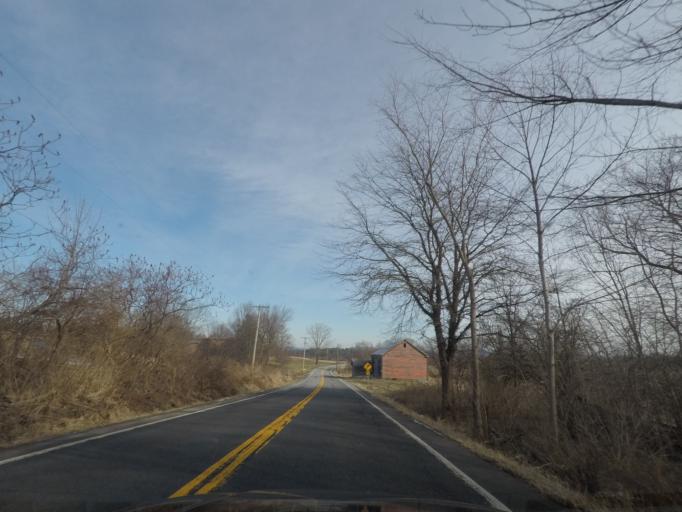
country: US
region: New York
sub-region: Saratoga County
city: Stillwater
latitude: 42.9857
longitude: -73.6633
